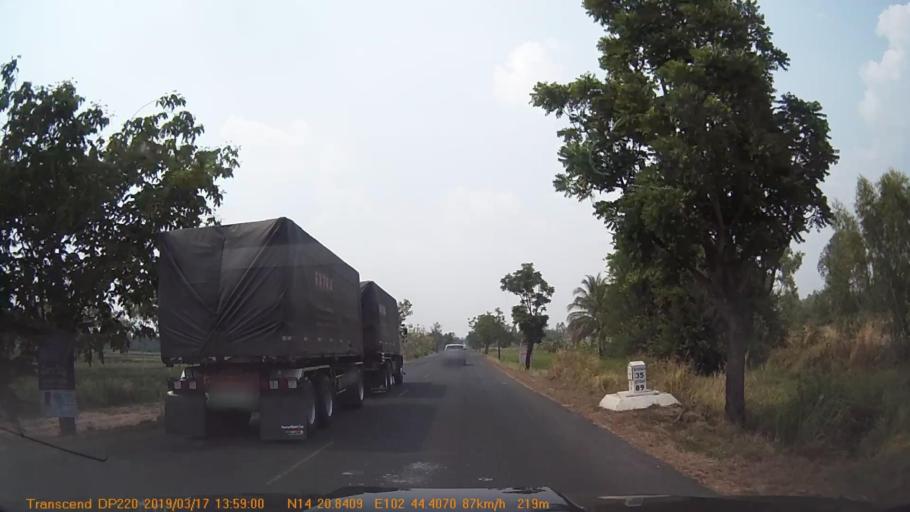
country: TH
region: Buriram
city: Non Din Daeng
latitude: 14.3475
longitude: 102.7400
